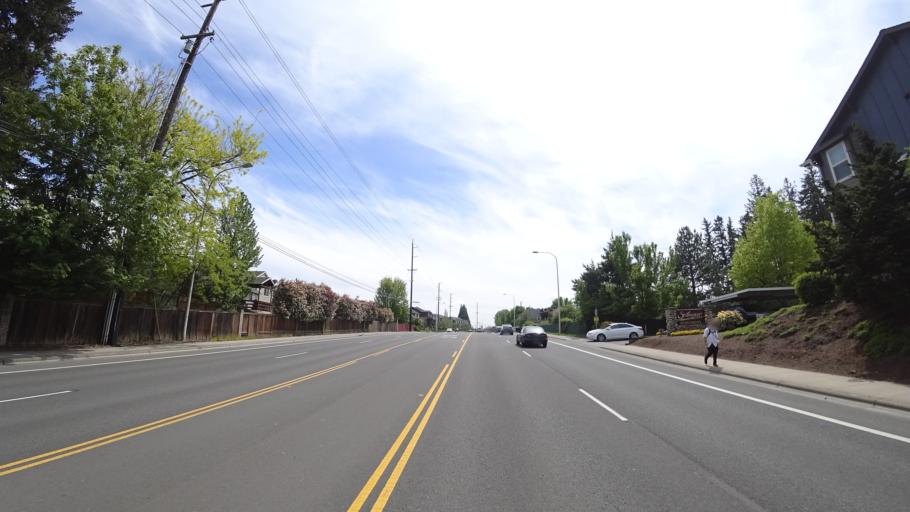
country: US
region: Oregon
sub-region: Washington County
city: Rockcreek
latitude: 45.5199
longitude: -122.8998
